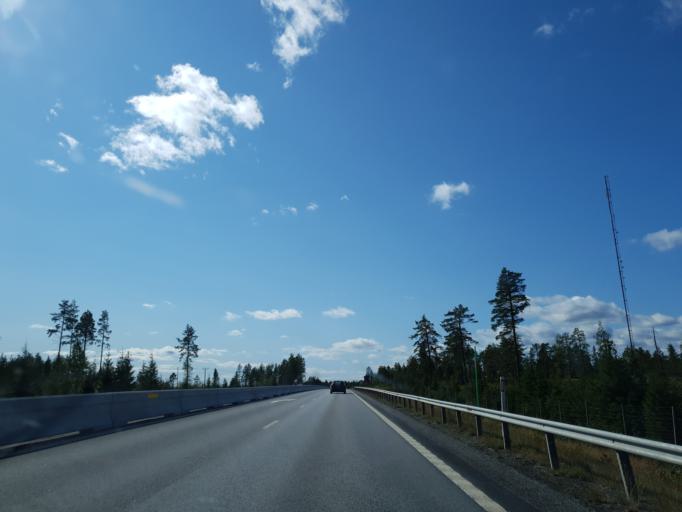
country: SE
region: Vaesterbotten
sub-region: Umea Kommun
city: Hoernefors
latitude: 63.6533
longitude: 19.9515
